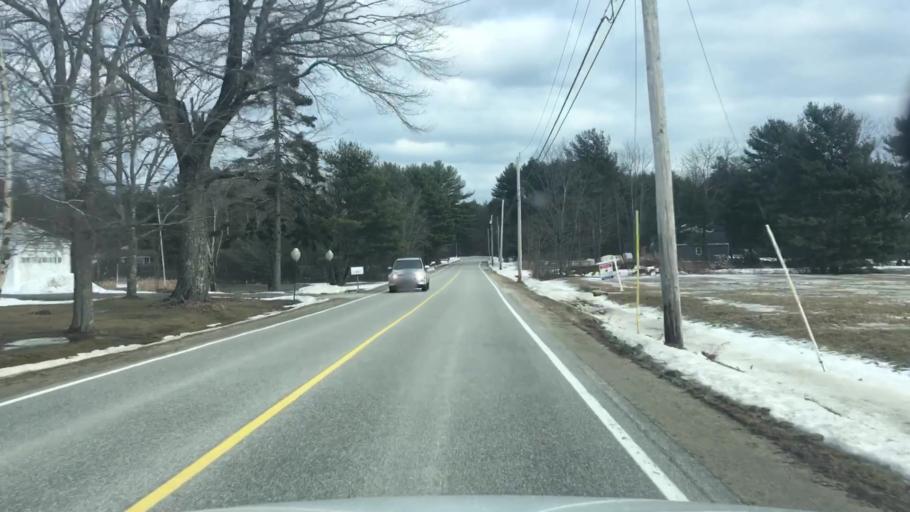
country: US
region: Maine
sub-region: York County
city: Arundel
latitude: 43.4075
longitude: -70.5042
